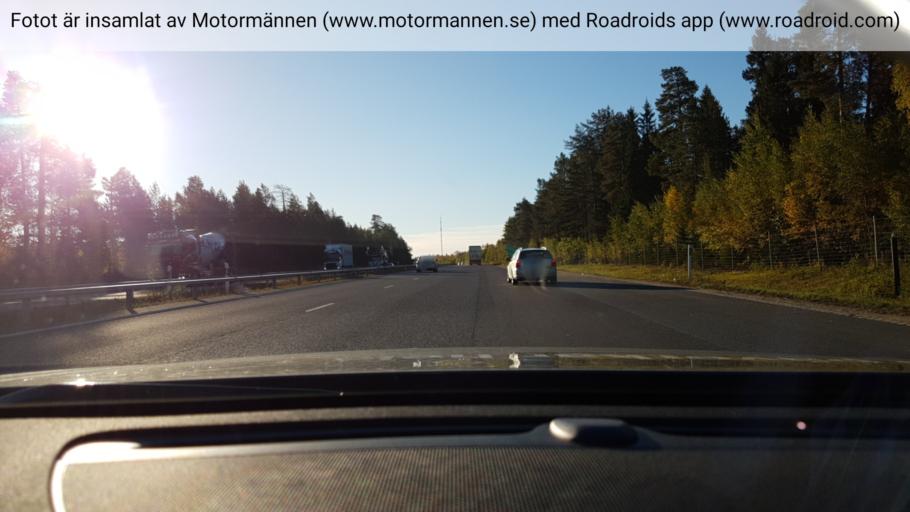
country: SE
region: Norrbotten
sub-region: Lulea Kommun
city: Gammelstad
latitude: 65.6323
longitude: 22.0377
